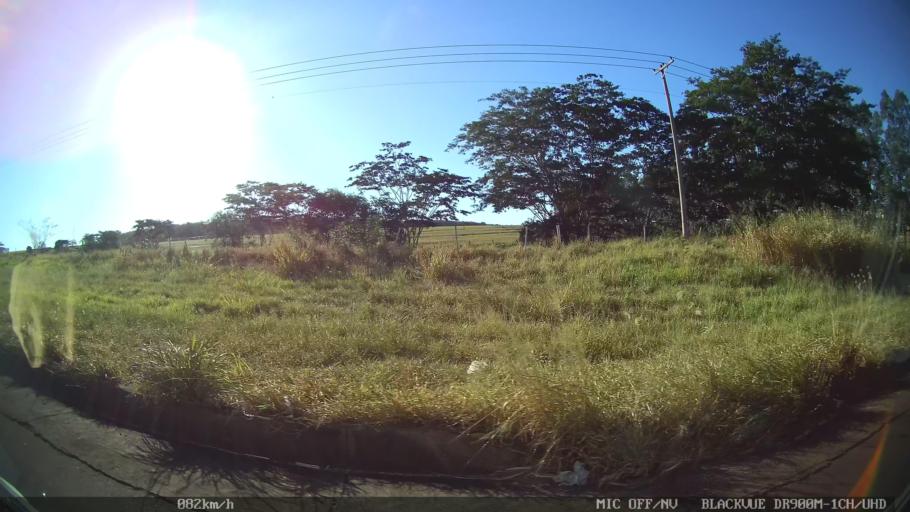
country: BR
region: Sao Paulo
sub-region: Olimpia
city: Olimpia
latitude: -20.7147
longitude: -48.9926
